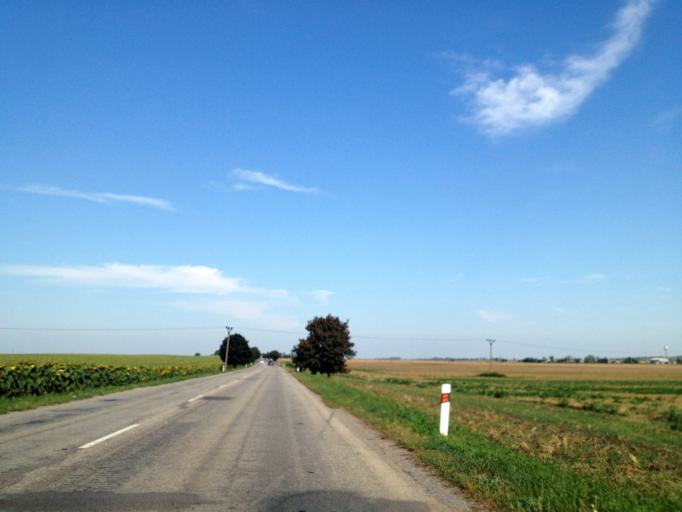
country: SK
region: Nitriansky
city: Svodin
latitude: 47.8899
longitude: 18.4057
